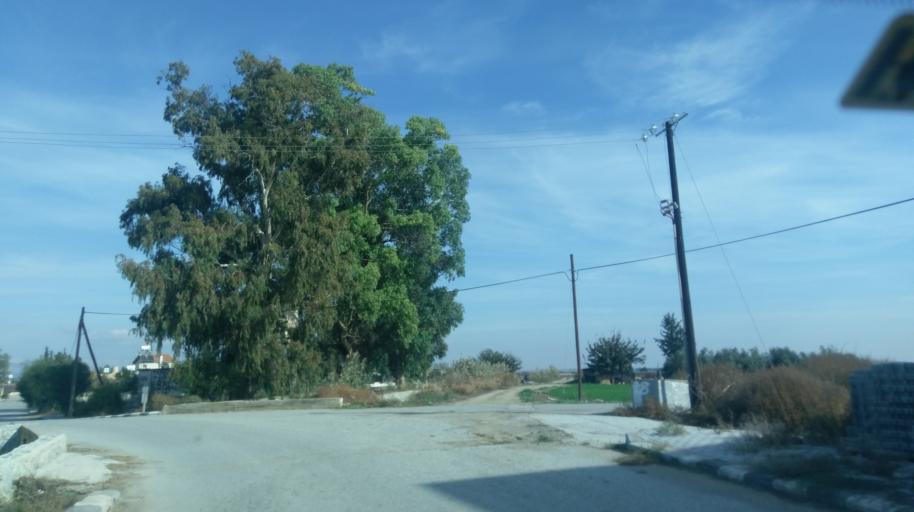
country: CY
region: Ammochostos
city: Lefkonoiko
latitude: 35.1910
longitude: 33.6399
